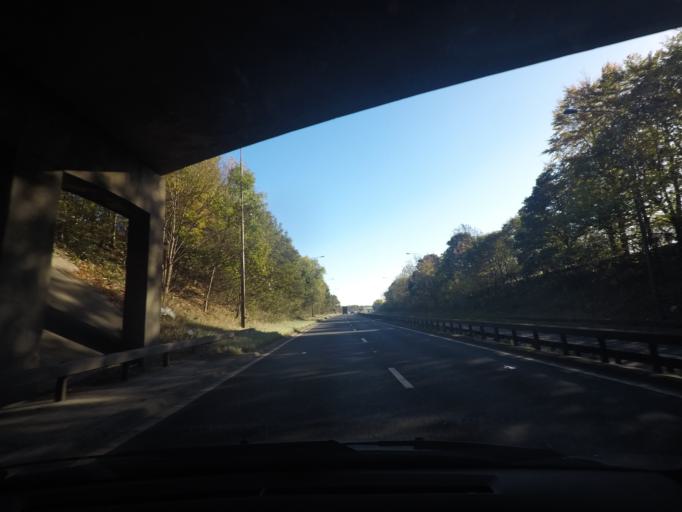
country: GB
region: England
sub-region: East Riding of Yorkshire
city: North Ferriby
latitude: 53.7263
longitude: -0.5014
